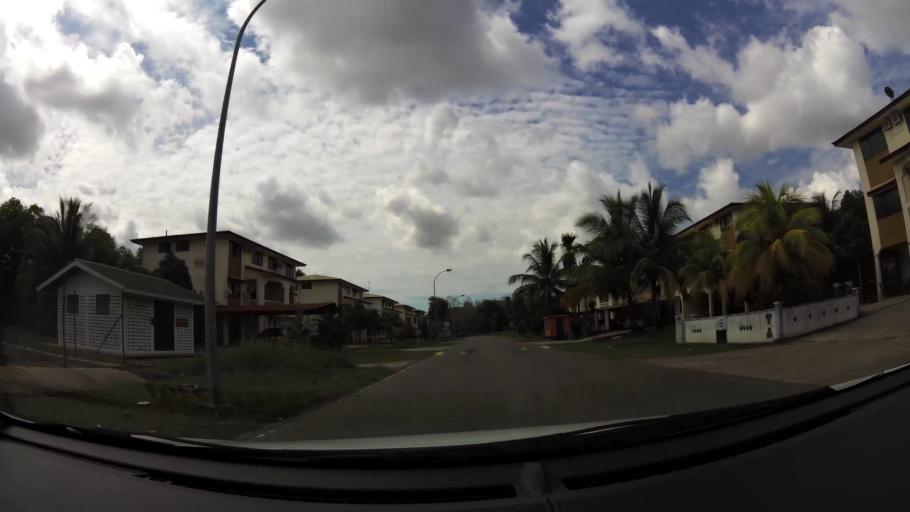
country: BN
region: Brunei and Muara
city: Bandar Seri Begawan
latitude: 4.9336
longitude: 114.8961
